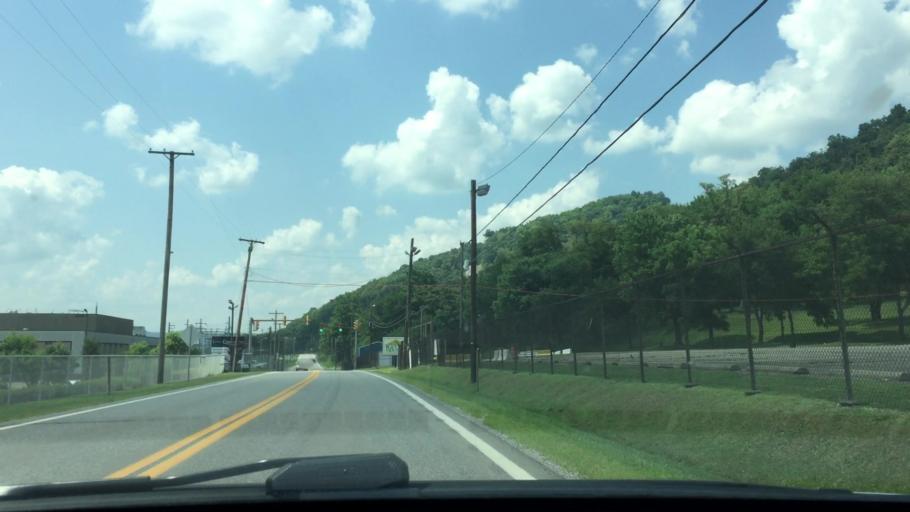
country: US
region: West Virginia
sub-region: Wetzel County
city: New Martinsville
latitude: 39.7256
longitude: -80.8265
